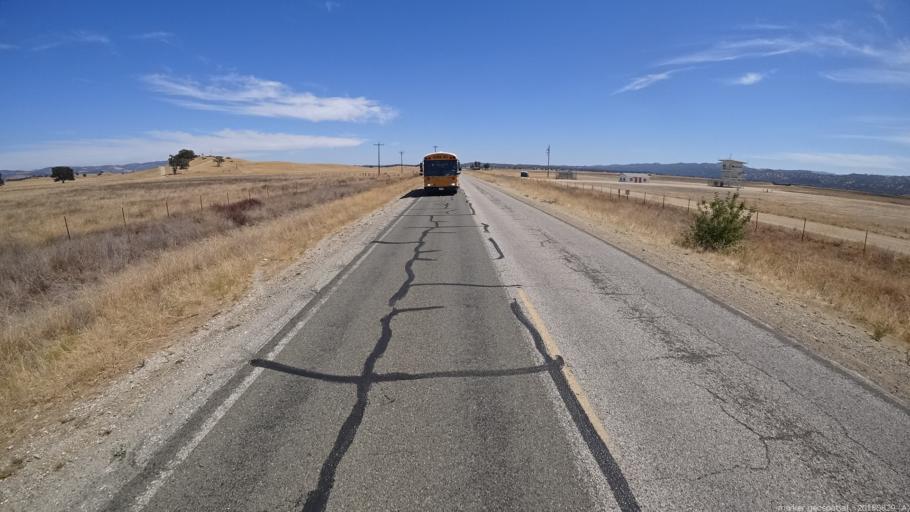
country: US
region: California
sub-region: Monterey County
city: King City
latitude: 35.9521
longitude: -121.1481
